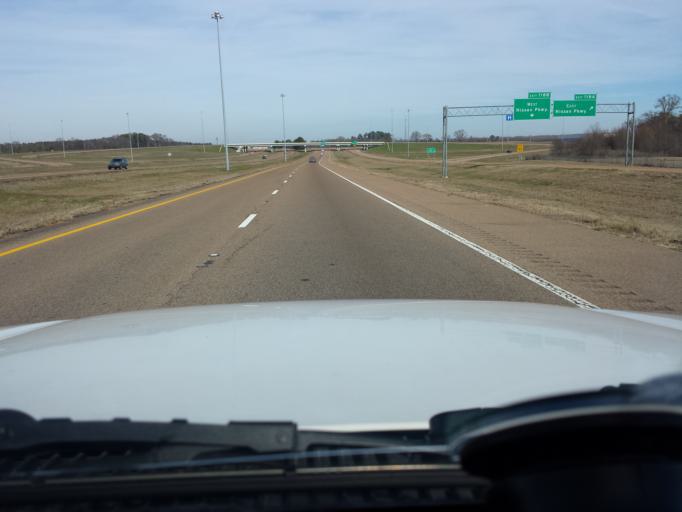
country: US
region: Mississippi
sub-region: Madison County
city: Canton
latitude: 32.5807
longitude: -90.0717
